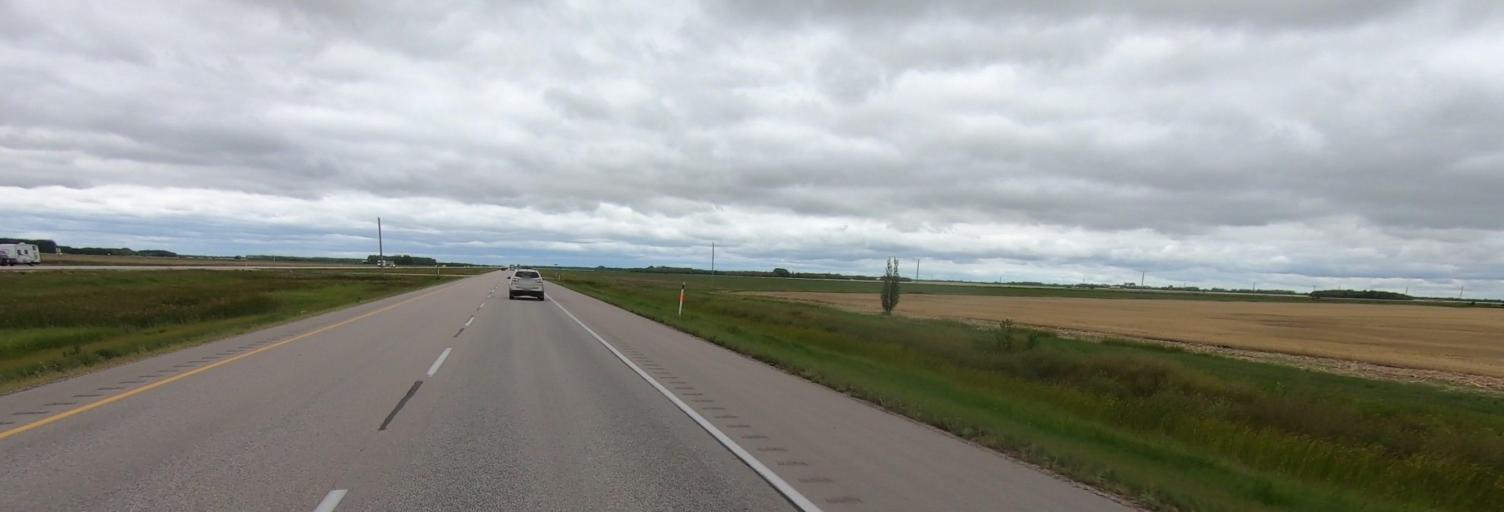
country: CA
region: Manitoba
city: Portage la Prairie
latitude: 49.9406
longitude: -97.9388
